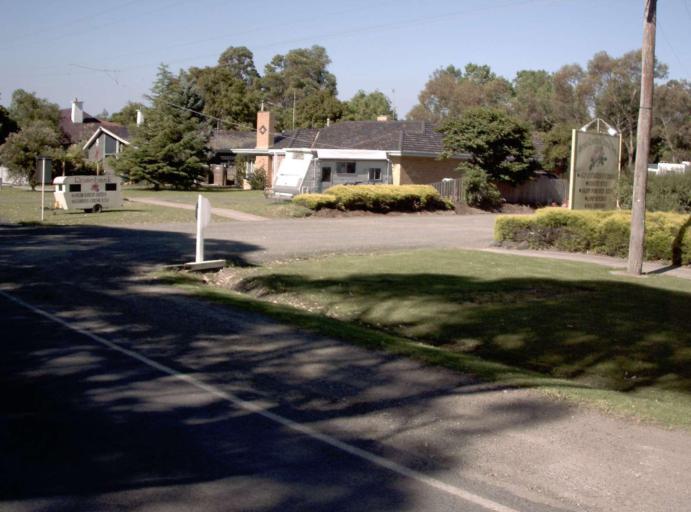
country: AU
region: Victoria
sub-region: Latrobe
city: Traralgon
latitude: -38.5695
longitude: 146.6746
